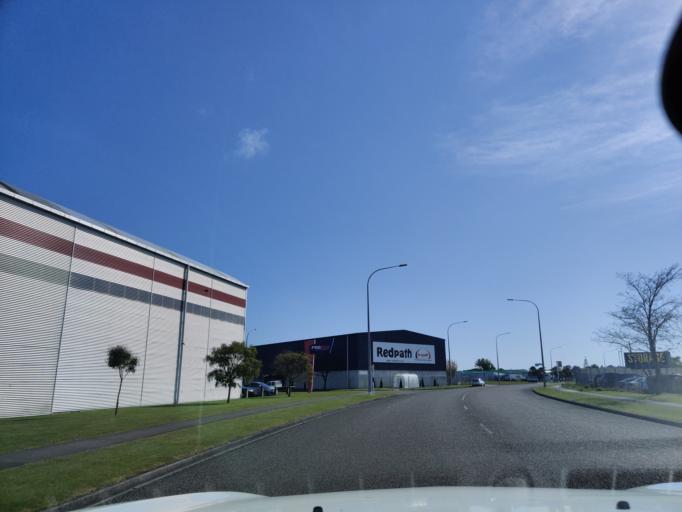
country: NZ
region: Manawatu-Wanganui
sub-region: Palmerston North City
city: Palmerston North
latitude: -40.3350
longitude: 175.6447
